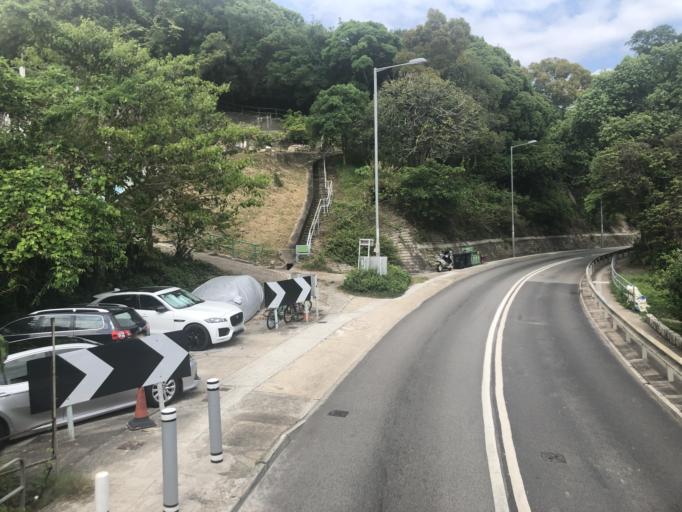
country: HK
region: Sai Kung
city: Sai Kung
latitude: 22.3952
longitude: 114.2786
